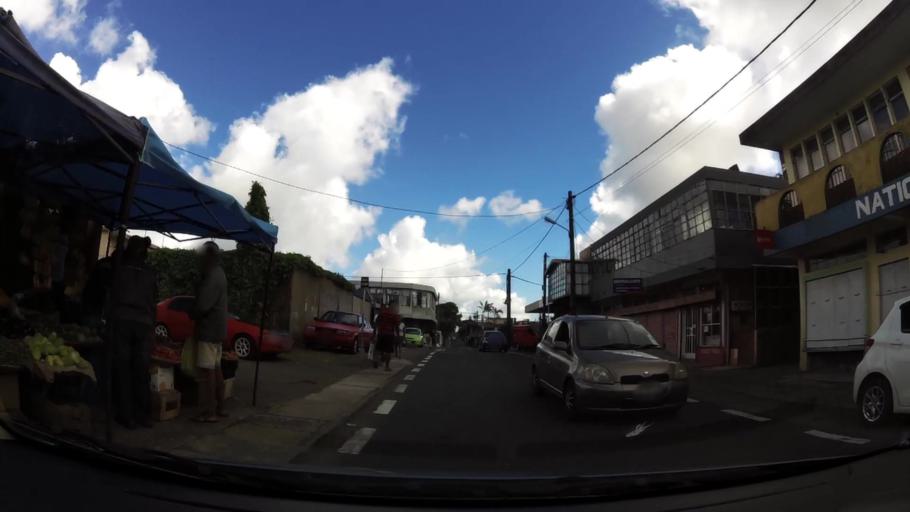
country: MU
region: Plaines Wilhems
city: Curepipe
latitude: -20.3295
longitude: 57.5267
